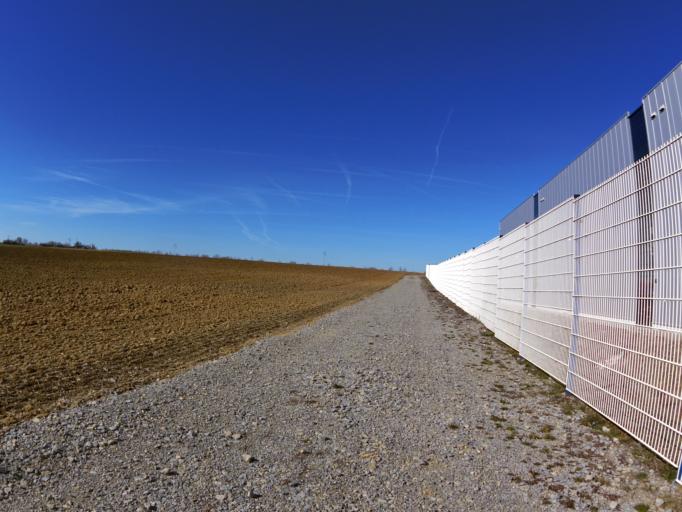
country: DE
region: Bavaria
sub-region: Regierungsbezirk Unterfranken
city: Kurnach
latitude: 49.8524
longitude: 10.0247
